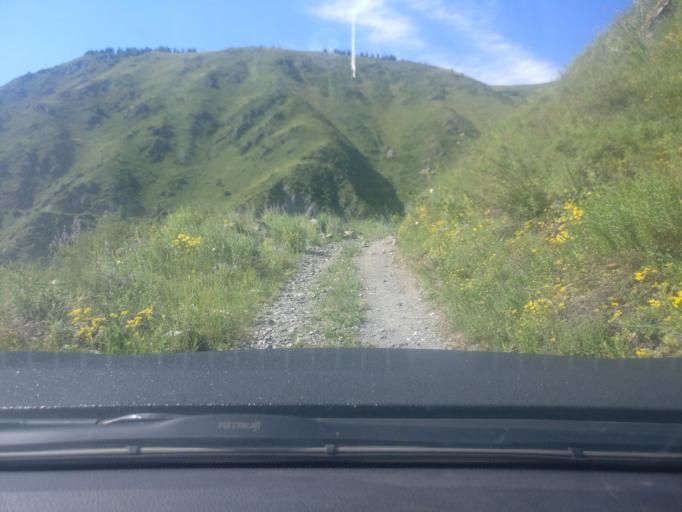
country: KZ
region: Almaty Qalasy
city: Almaty
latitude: 43.1031
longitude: 76.9504
